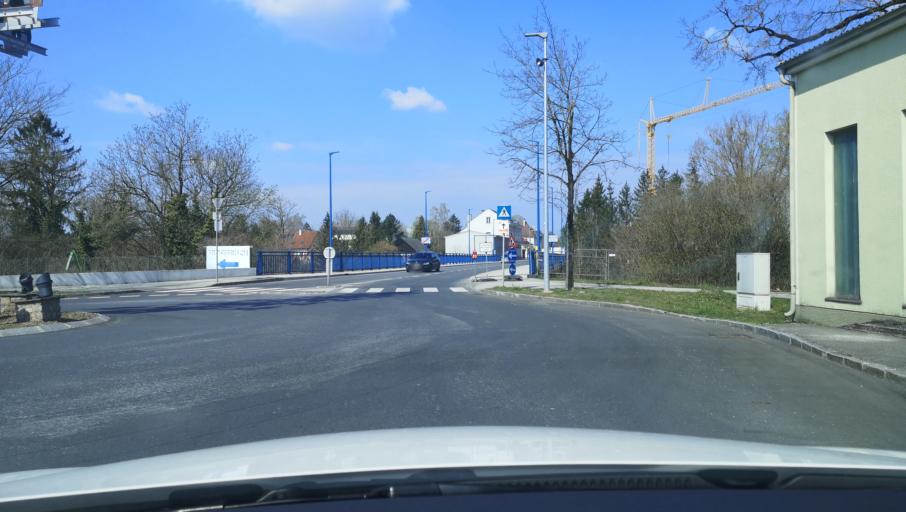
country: AT
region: Lower Austria
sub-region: Politischer Bezirk Amstetten
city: Winklarn
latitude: 48.0770
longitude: 14.8154
